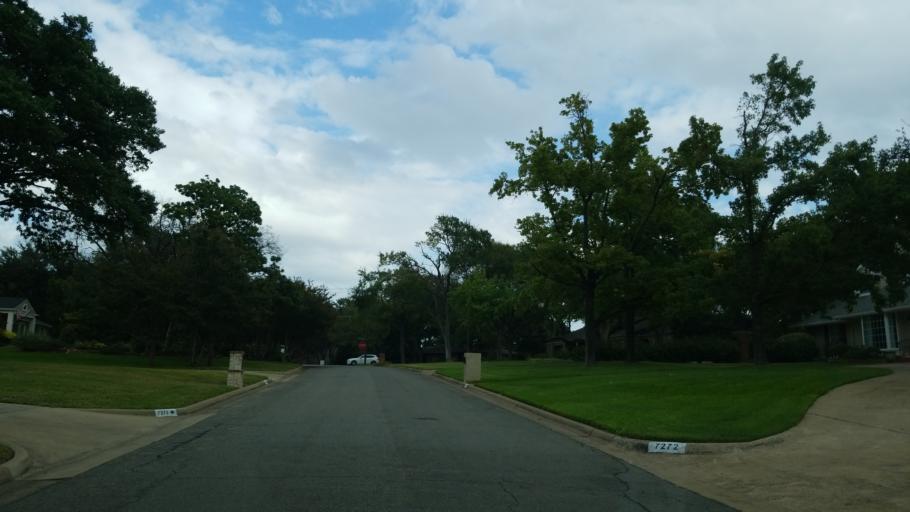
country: US
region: Texas
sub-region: Dallas County
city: Richardson
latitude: 32.9392
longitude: -96.7798
